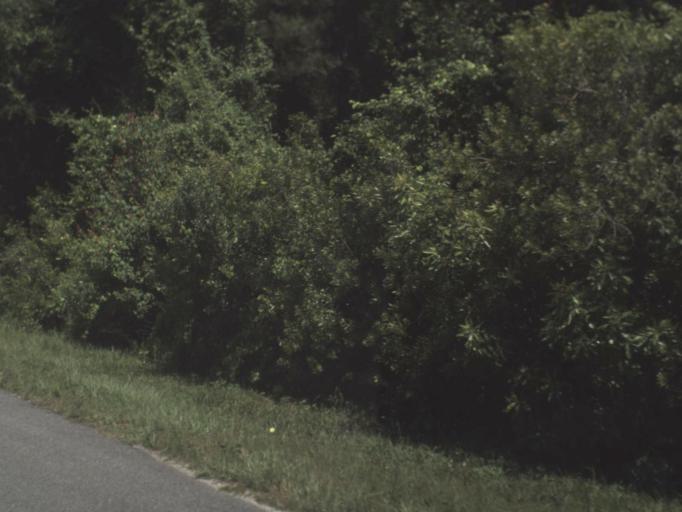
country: US
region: Florida
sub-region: Suwannee County
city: Wellborn
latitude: 30.2435
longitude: -82.8686
